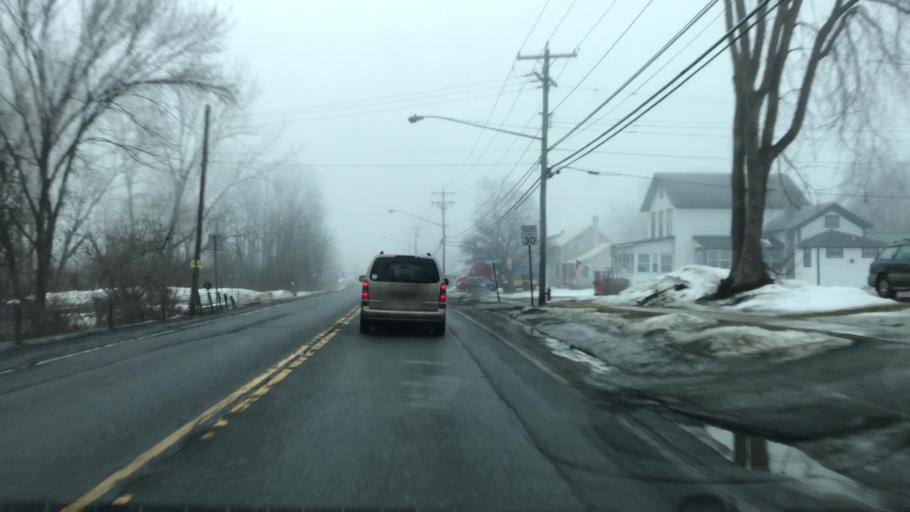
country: US
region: New York
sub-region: Washington County
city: Whitehall
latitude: 43.5434
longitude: -73.4077
